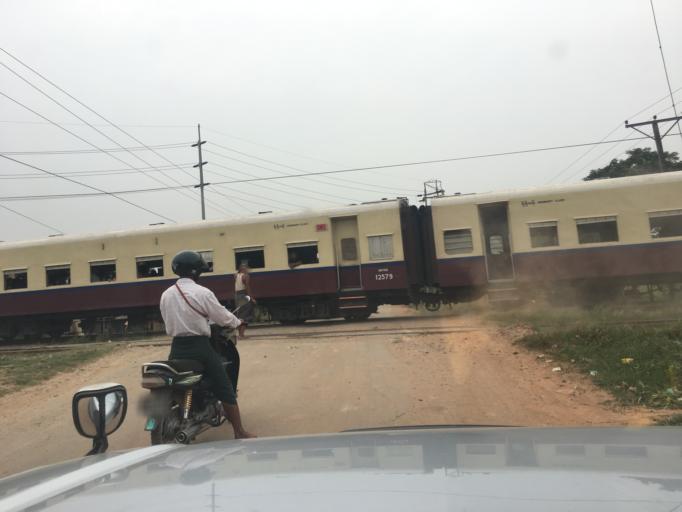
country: MM
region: Yangon
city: Syriam
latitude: 16.9490
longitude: 96.2786
